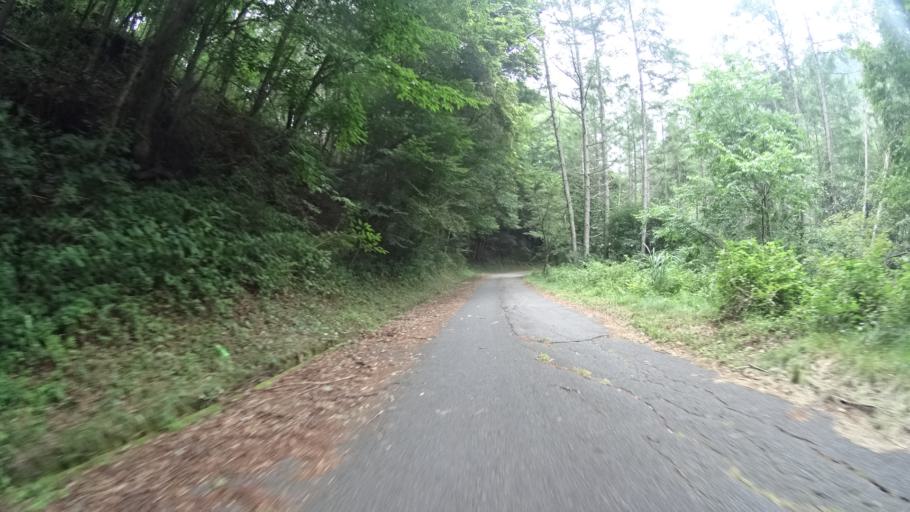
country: JP
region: Yamanashi
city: Kofu-shi
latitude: 35.8222
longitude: 138.5958
